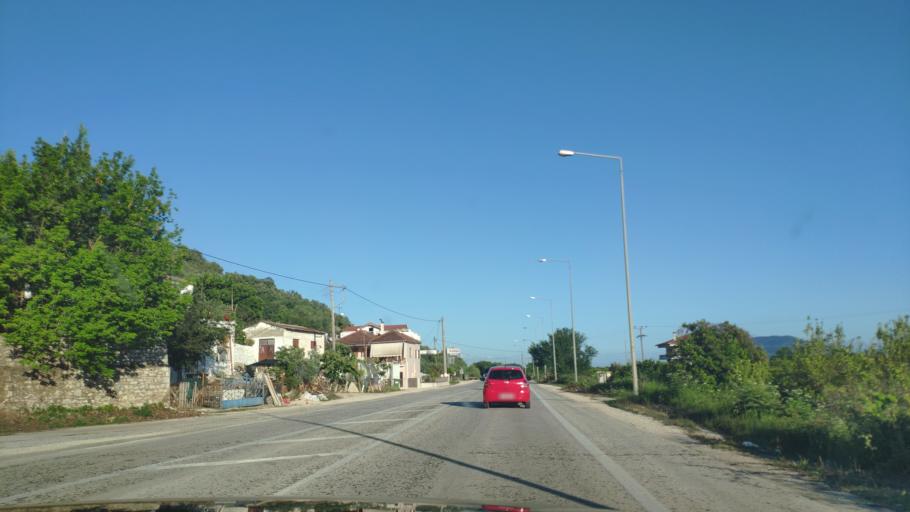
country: GR
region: Epirus
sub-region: Nomos Prevezis
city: Louros
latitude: 39.1770
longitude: 20.7893
